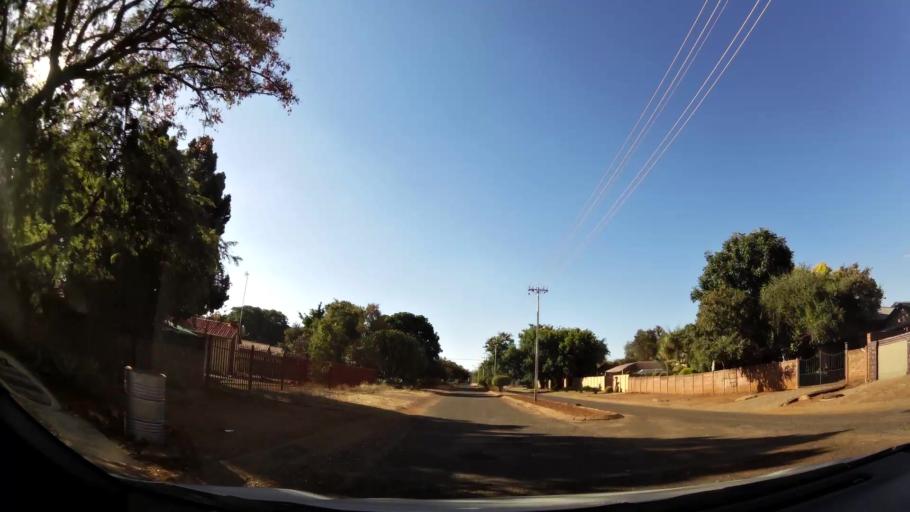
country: ZA
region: Limpopo
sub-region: Waterberg District Municipality
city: Mokopane
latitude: -24.2091
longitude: 29.0069
